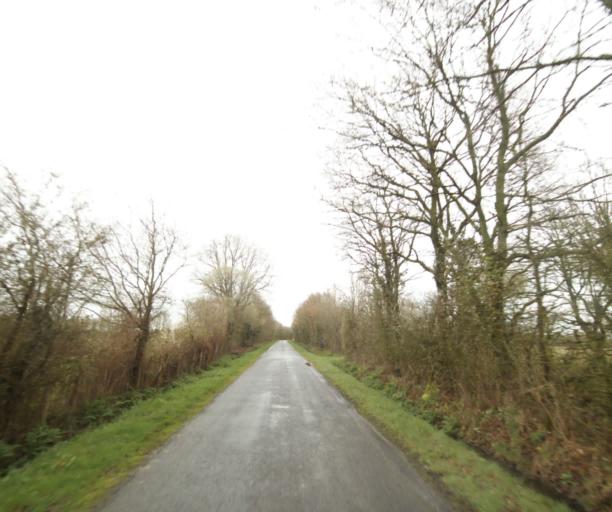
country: FR
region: Pays de la Loire
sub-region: Departement de la Loire-Atlantique
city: Bouvron
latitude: 47.4542
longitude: -1.8785
